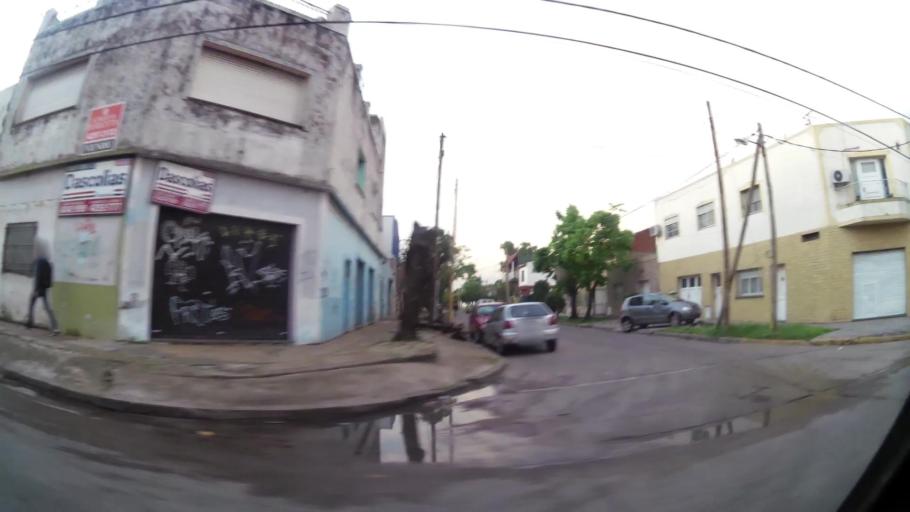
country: AR
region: Buenos Aires
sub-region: Partido de Lomas de Zamora
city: Lomas de Zamora
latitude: -34.7519
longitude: -58.3685
